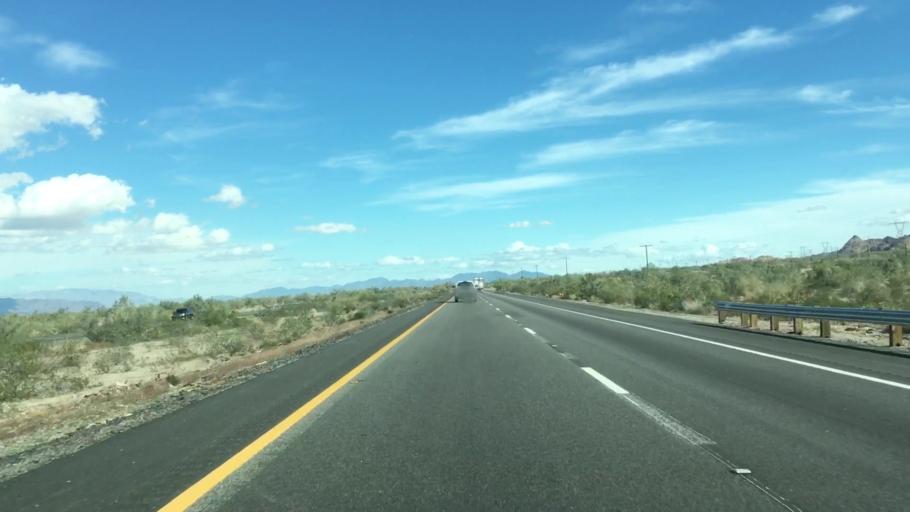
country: US
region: California
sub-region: Imperial County
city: Niland
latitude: 33.6923
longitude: -115.4975
